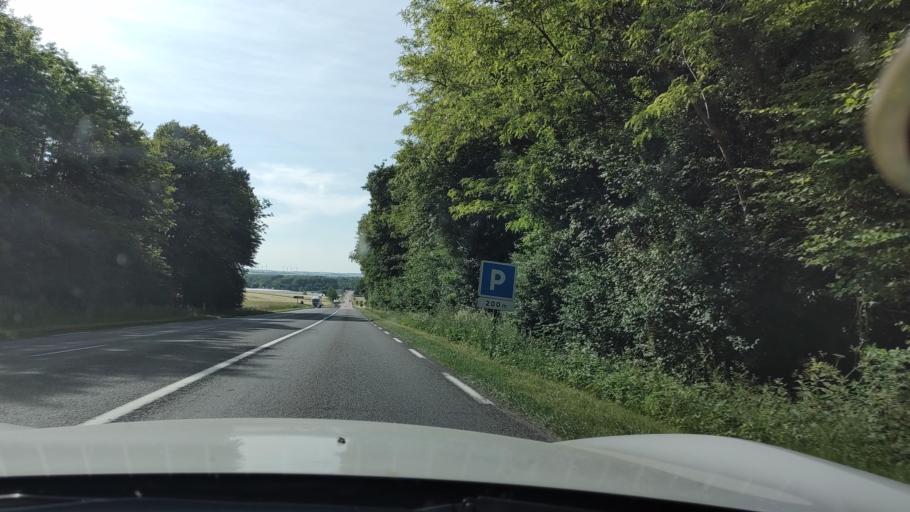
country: FR
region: Ile-de-France
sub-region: Departement de Seine-et-Marne
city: Sourdun
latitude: 48.5189
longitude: 3.4183
